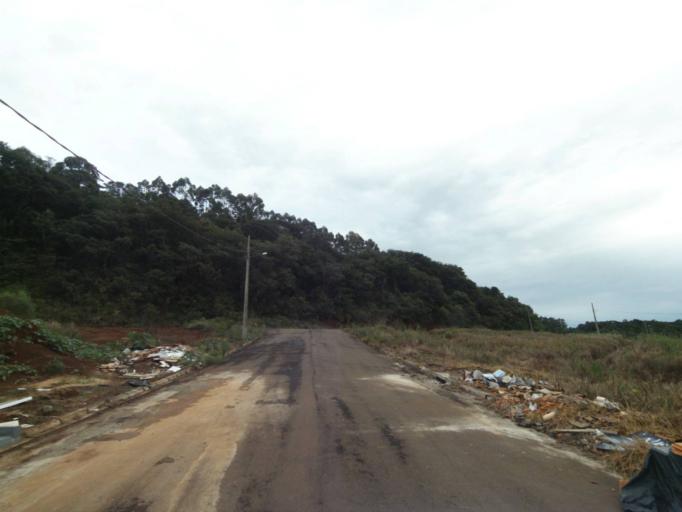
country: BR
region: Parana
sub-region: Guaraniacu
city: Guaraniacu
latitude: -25.1007
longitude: -52.8883
